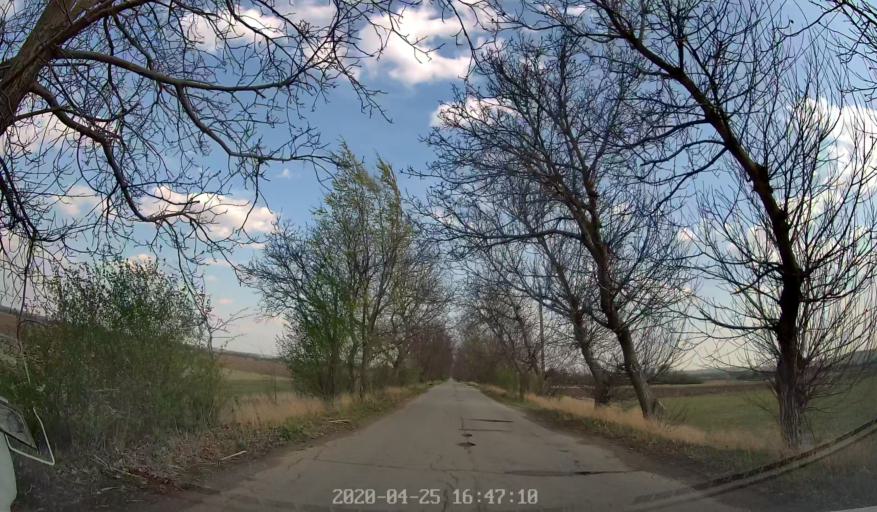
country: MD
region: Chisinau
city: Vadul lui Voda
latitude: 47.1383
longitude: 29.0714
